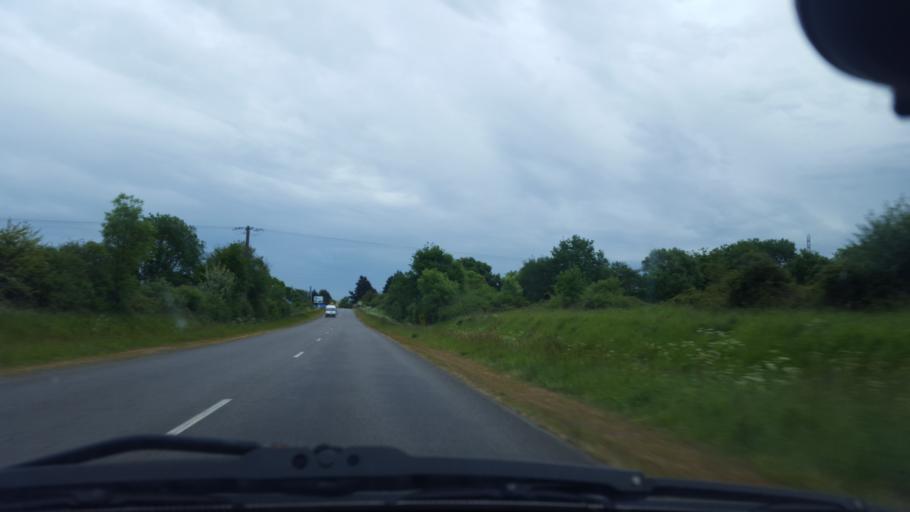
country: FR
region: Pays de la Loire
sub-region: Departement de la Loire-Atlantique
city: Les Sorinieres
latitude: 47.1512
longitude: -1.5067
